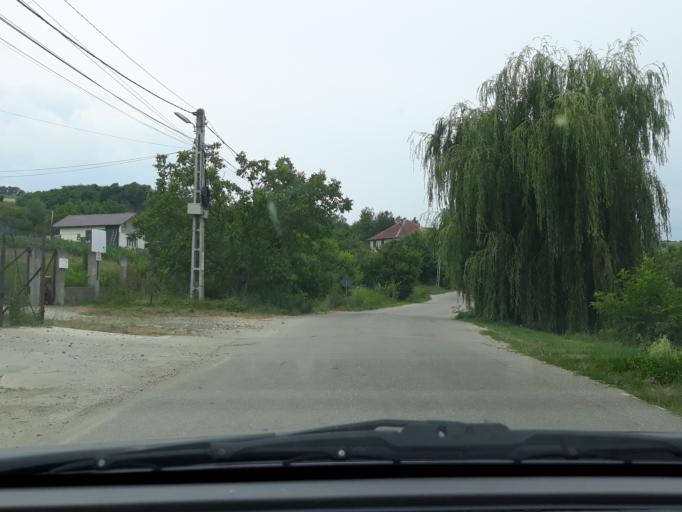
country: RO
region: Salaj
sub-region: Comuna Criseni
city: Criseni
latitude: 47.2496
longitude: 23.0714
